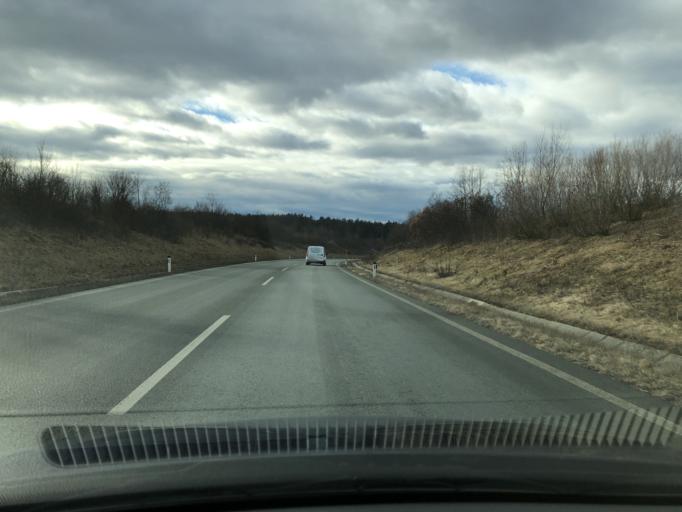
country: AT
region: Burgenland
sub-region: Politischer Bezirk Oberwart
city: Markt Neuhodis
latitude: 47.2650
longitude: 16.3776
